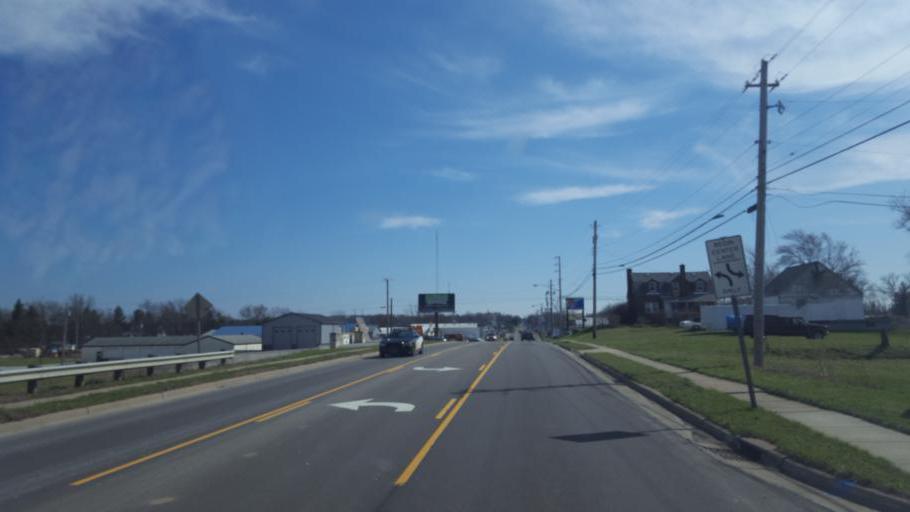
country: US
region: Ohio
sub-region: Richland County
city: Mansfield
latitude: 40.7700
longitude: -82.5518
